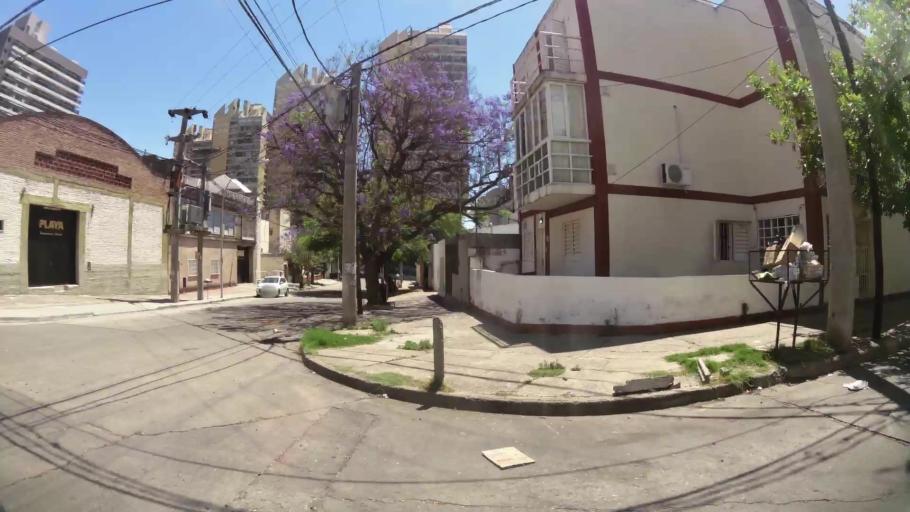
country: AR
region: Cordoba
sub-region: Departamento de Capital
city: Cordoba
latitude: -31.4101
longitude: -64.2072
